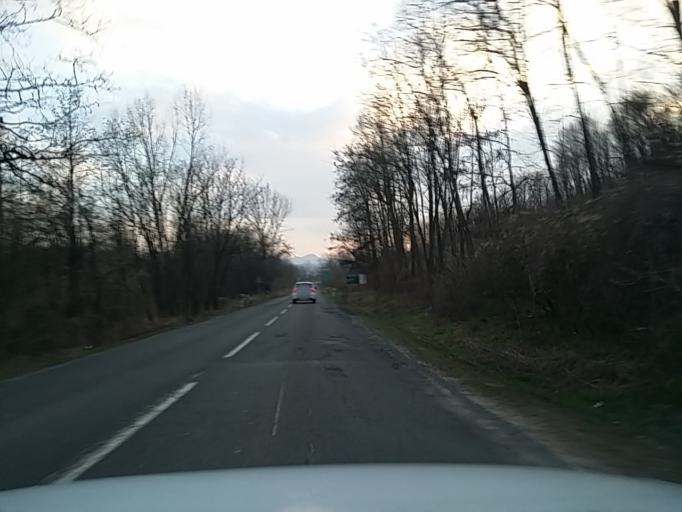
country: HU
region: Nograd
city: Matraterenye
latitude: 48.0046
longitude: 19.9245
